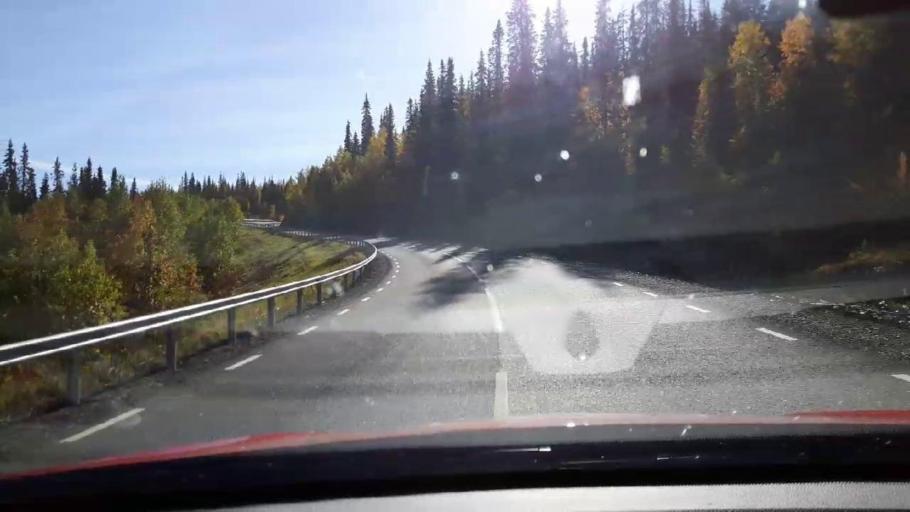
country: NO
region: Nord-Trondelag
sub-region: Royrvik
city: Royrvik
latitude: 64.8519
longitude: 14.1776
